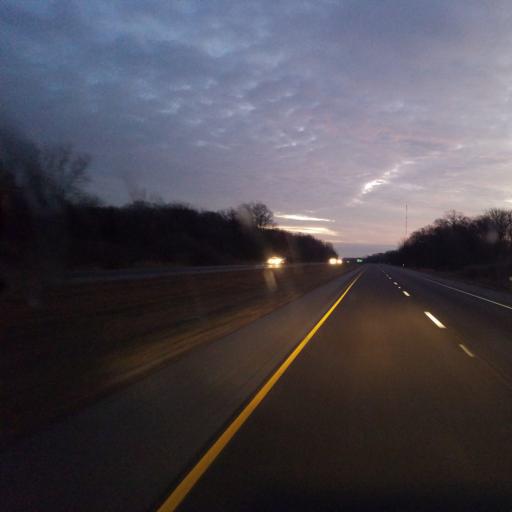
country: US
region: Illinois
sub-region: Tazewell County
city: Creve Coeur
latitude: 40.6303
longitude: -89.5671
